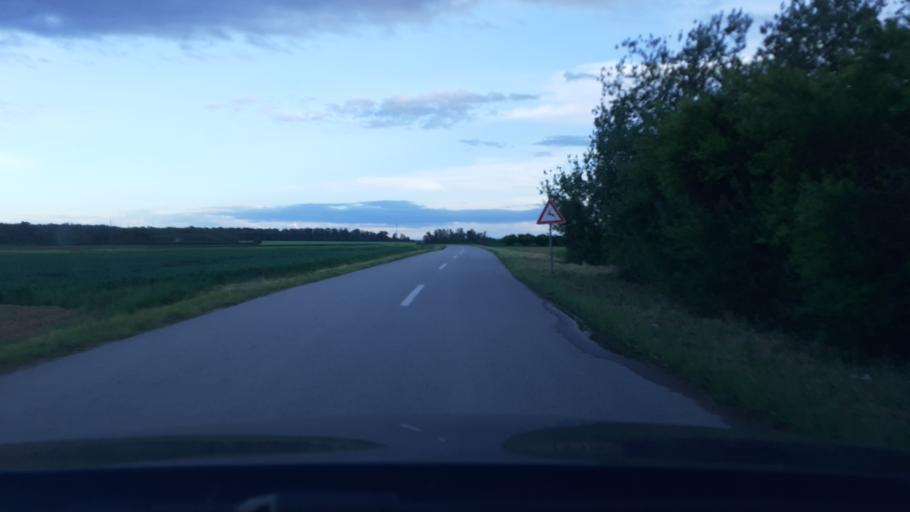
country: HR
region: Pozesko-Slavonska
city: Jaksic
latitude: 45.3572
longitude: 17.7746
